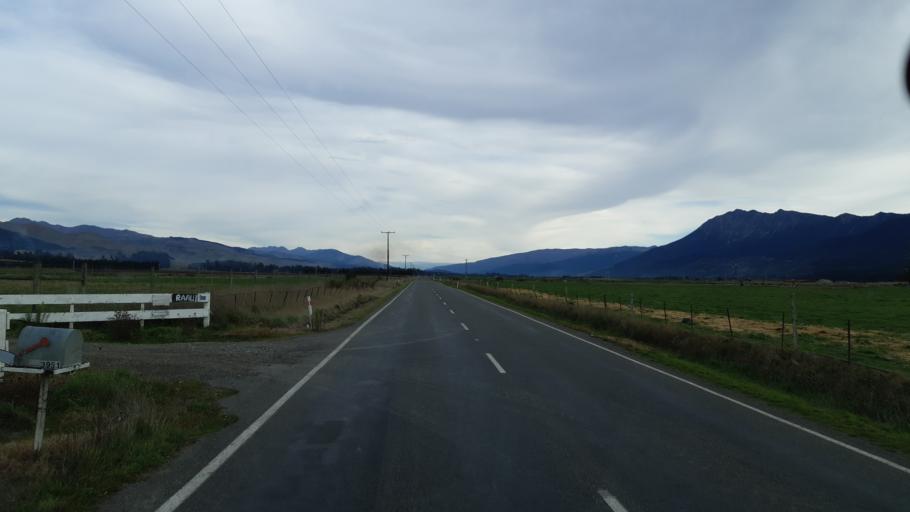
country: NZ
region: Tasman
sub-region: Tasman District
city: Richmond
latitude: -41.6101
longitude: 173.3973
